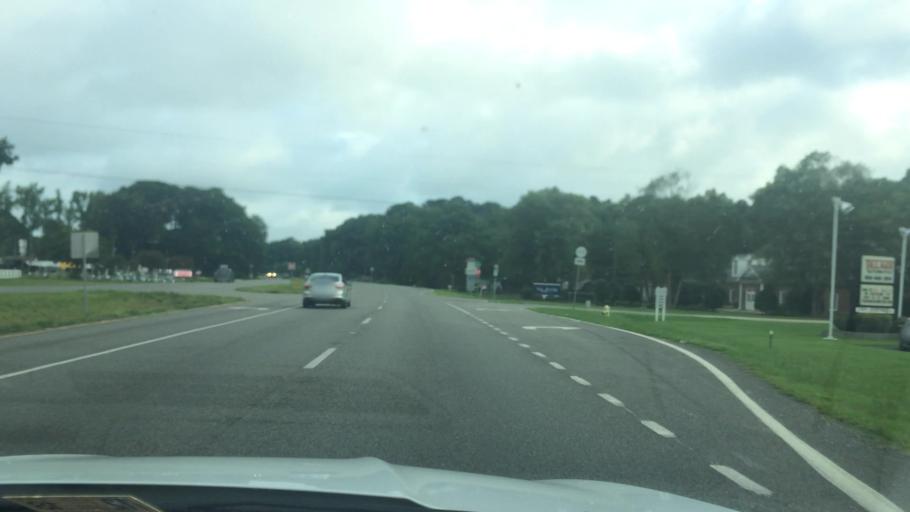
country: US
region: Virginia
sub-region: Gloucester County
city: Gloucester Point
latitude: 37.2638
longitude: -76.4936
